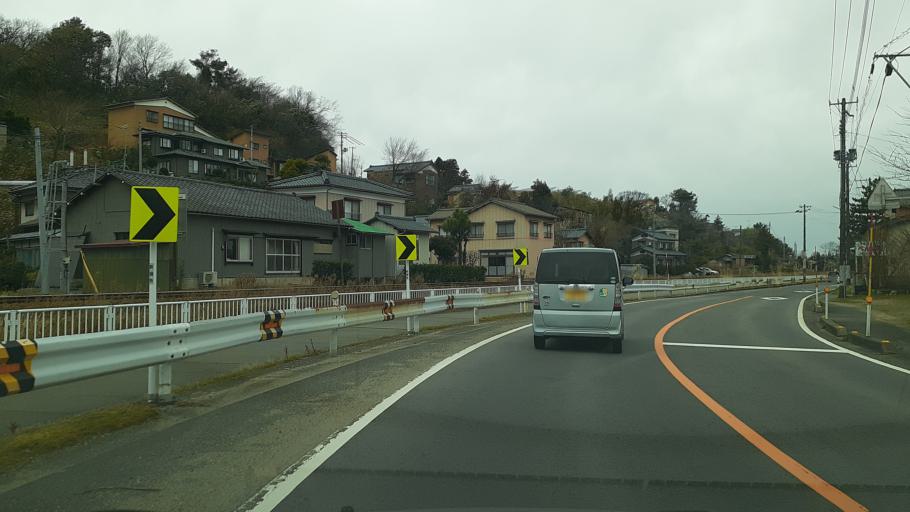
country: JP
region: Niigata
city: Niitsu-honcho
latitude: 37.7904
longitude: 139.1391
